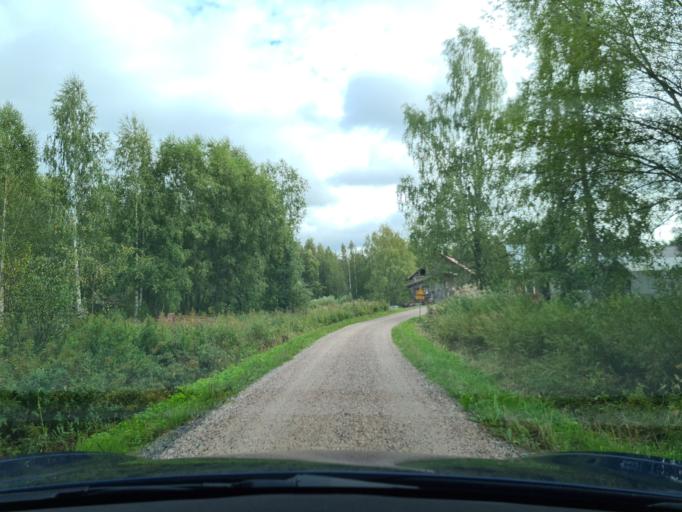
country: FI
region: Uusimaa
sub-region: Helsinki
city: Vihti
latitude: 60.4126
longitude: 24.4934
